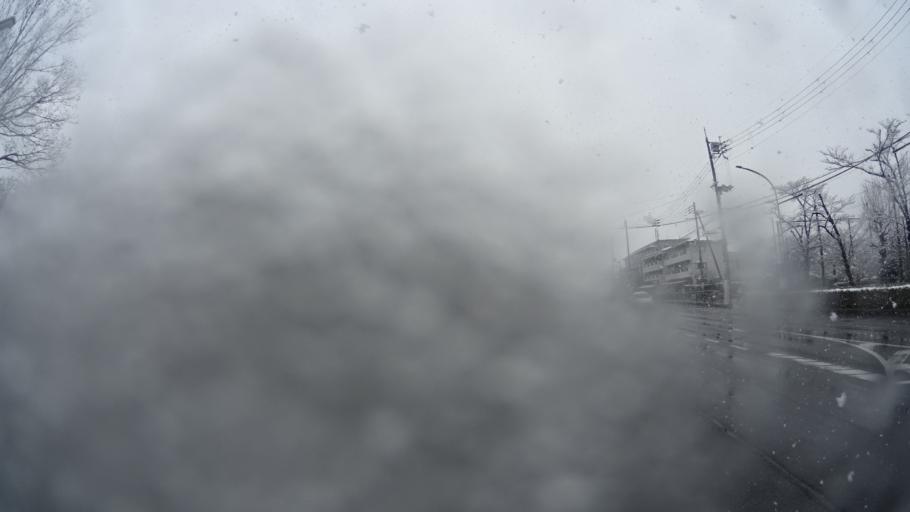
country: JP
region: Kyoto
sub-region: Kyoto-shi
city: Kamigyo-ku
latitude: 35.0646
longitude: 135.7850
